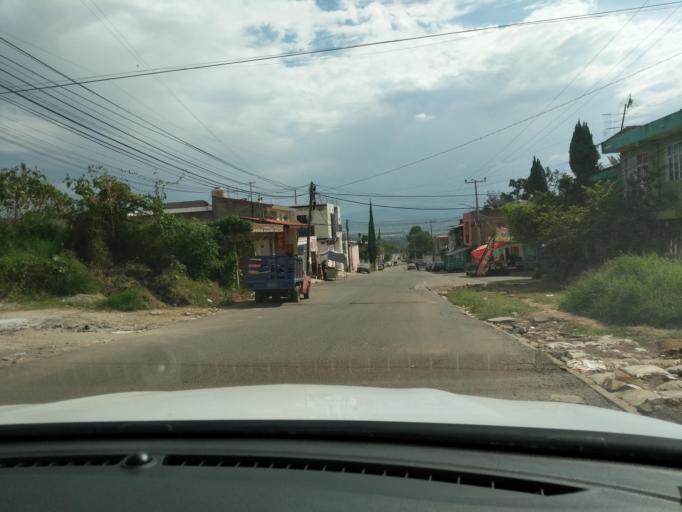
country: MX
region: Jalisco
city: San Jose del Castillo
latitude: 20.5192
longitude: -103.2348
